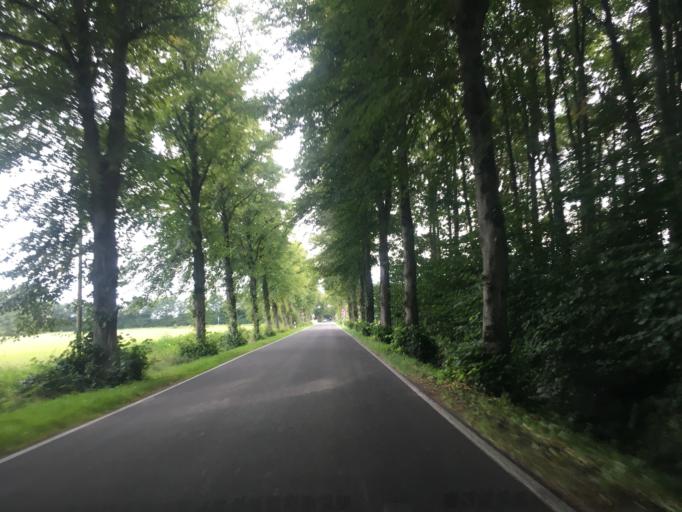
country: DE
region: North Rhine-Westphalia
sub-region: Regierungsbezirk Munster
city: Havixbeck
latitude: 51.9549
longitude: 7.5093
